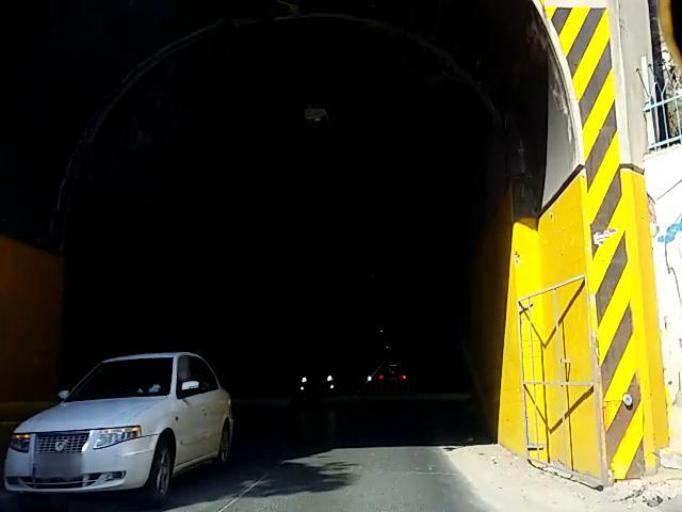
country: IR
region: Alborz
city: Karaj
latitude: 35.9545
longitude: 51.0861
